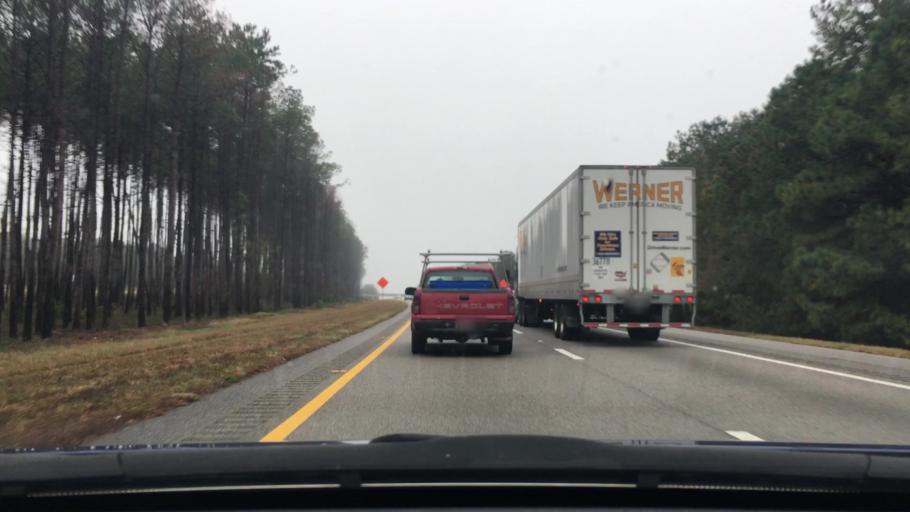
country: US
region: South Carolina
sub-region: Kershaw County
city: Camden
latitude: 34.2158
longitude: -80.5110
